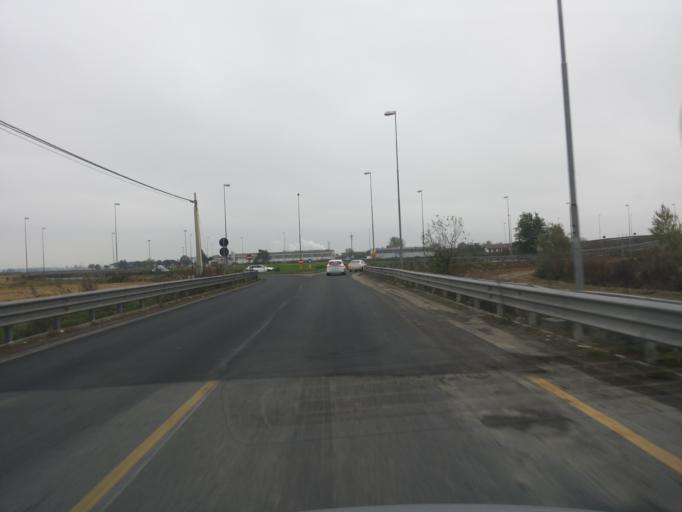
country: IT
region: Piedmont
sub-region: Provincia di Novara
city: Lumellogno
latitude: 45.4184
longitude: 8.5700
